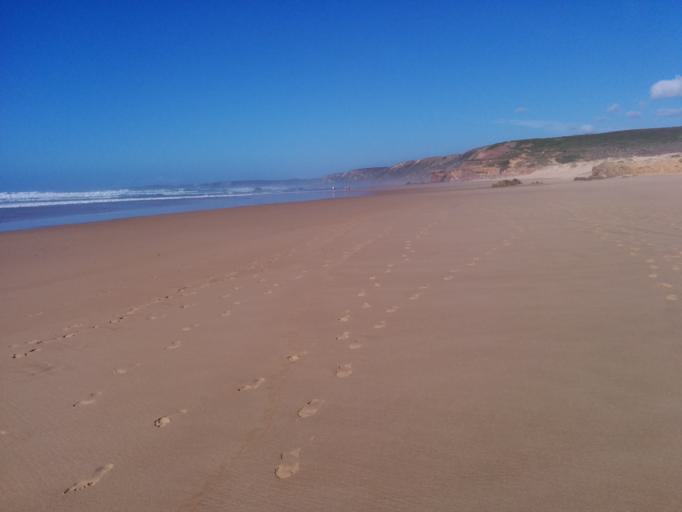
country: PT
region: Faro
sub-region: Vila do Bispo
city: Vila do Bispo
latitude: 37.2018
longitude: -8.9002
